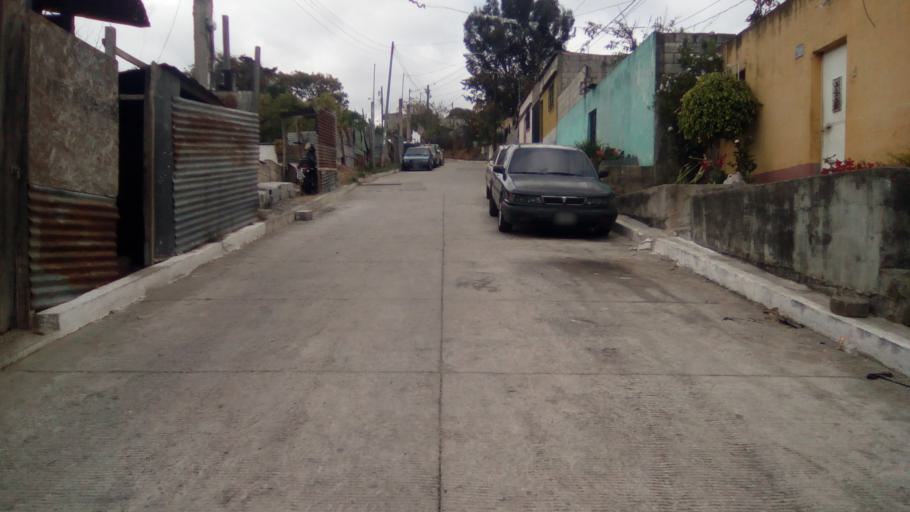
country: GT
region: Guatemala
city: Mixco
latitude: 14.5821
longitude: -90.6043
